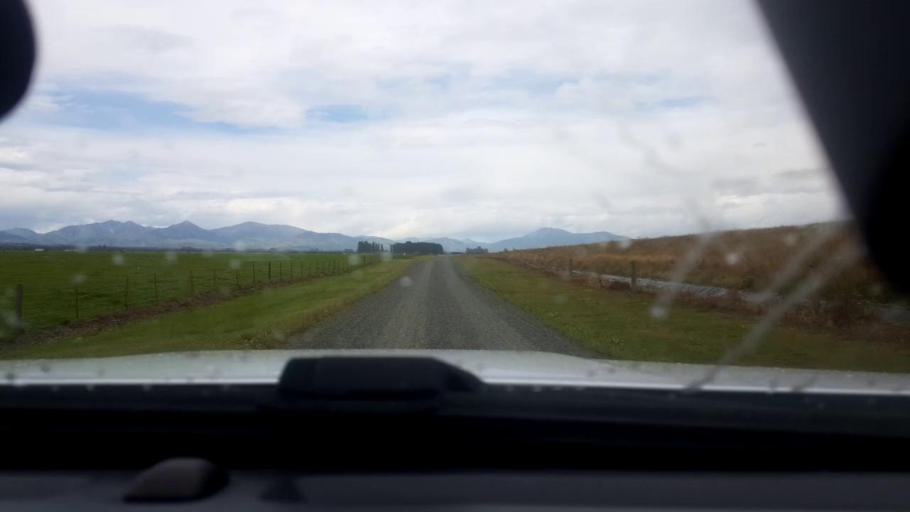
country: NZ
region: Canterbury
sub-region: Timaru District
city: Pleasant Point
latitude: -44.1190
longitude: 171.3597
